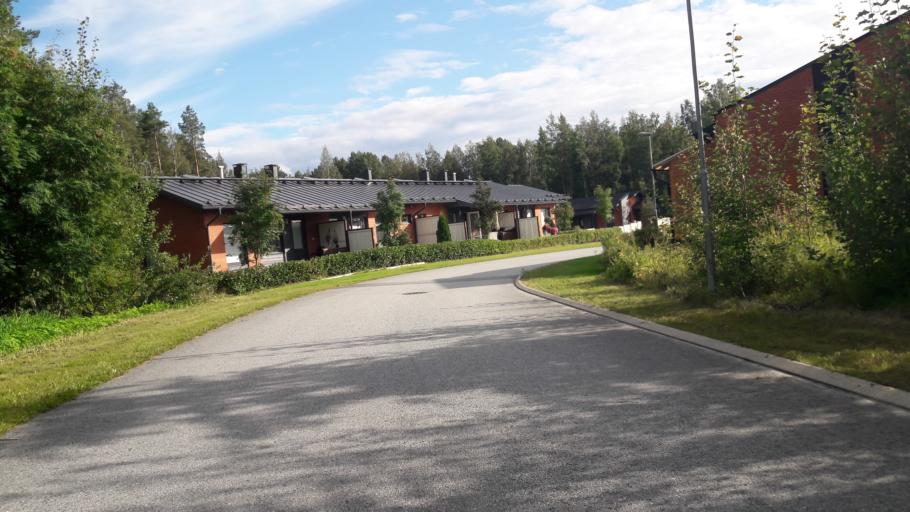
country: FI
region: North Karelia
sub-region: Joensuu
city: Joensuu
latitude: 62.5776
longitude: 29.7923
